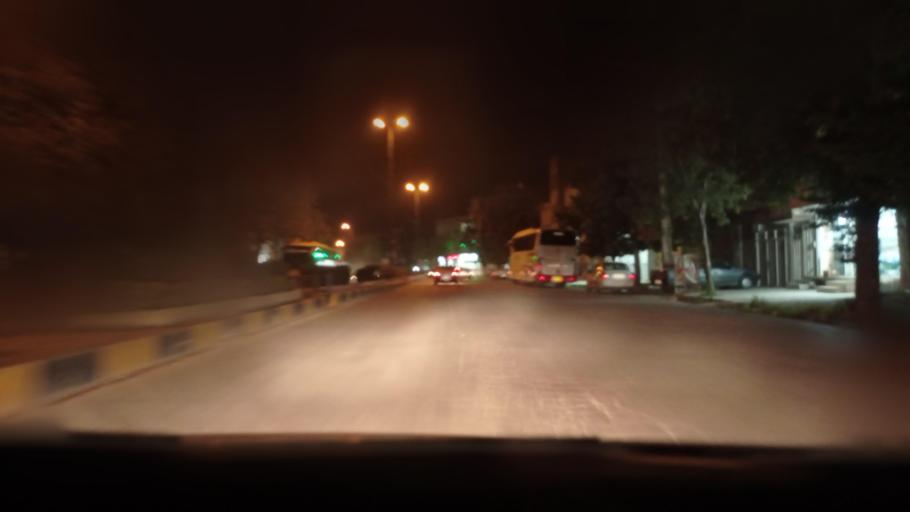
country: IR
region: Lorestan
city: Kuhdasht
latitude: 33.5382
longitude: 47.6110
